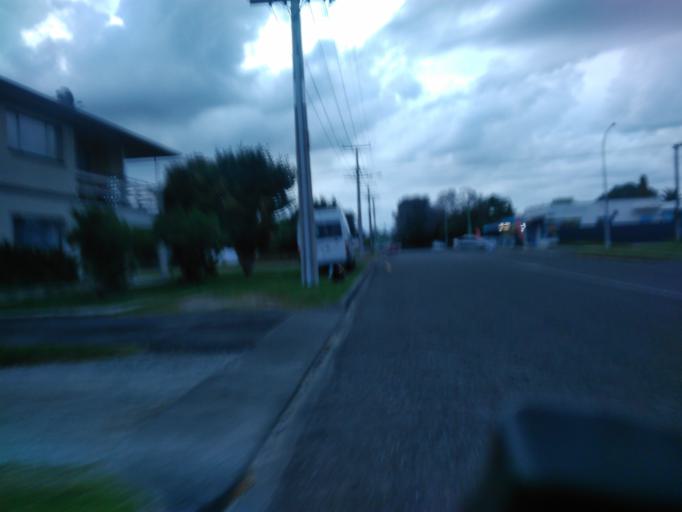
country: NZ
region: Gisborne
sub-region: Gisborne District
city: Gisborne
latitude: -38.6454
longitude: 178.0084
